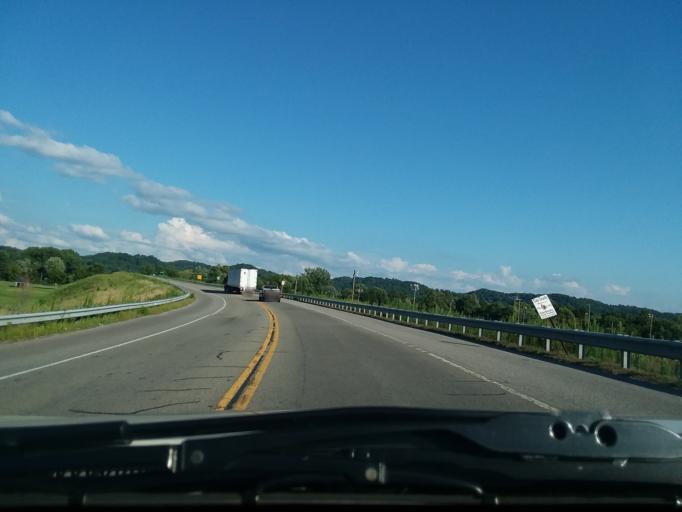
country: US
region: Tennessee
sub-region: Clay County
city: Celina
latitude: 36.5565
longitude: -85.5184
